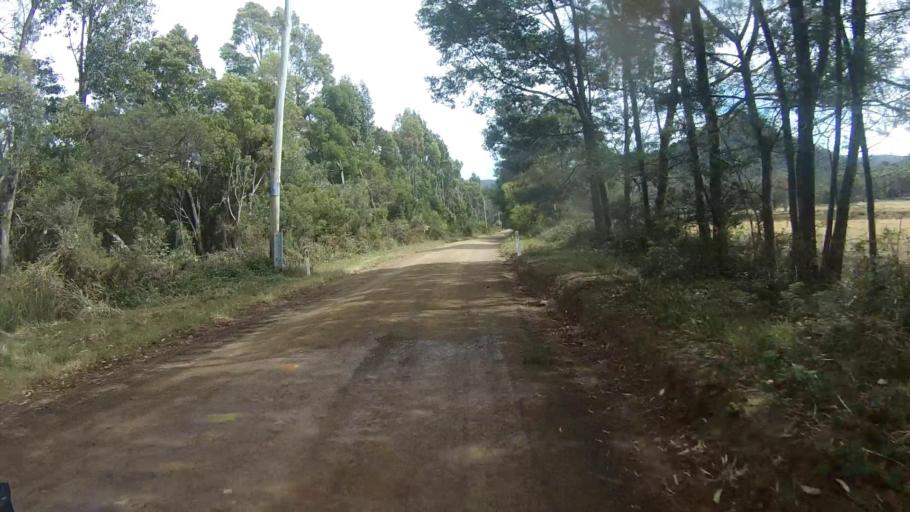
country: AU
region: Tasmania
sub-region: Sorell
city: Sorell
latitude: -42.7724
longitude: 147.8084
